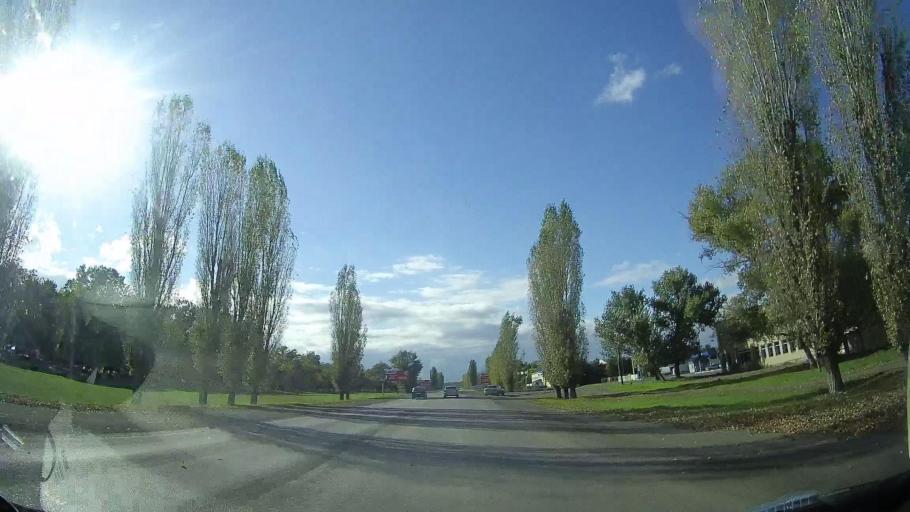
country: RU
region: Rostov
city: Tselina
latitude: 46.5321
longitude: 41.0035
